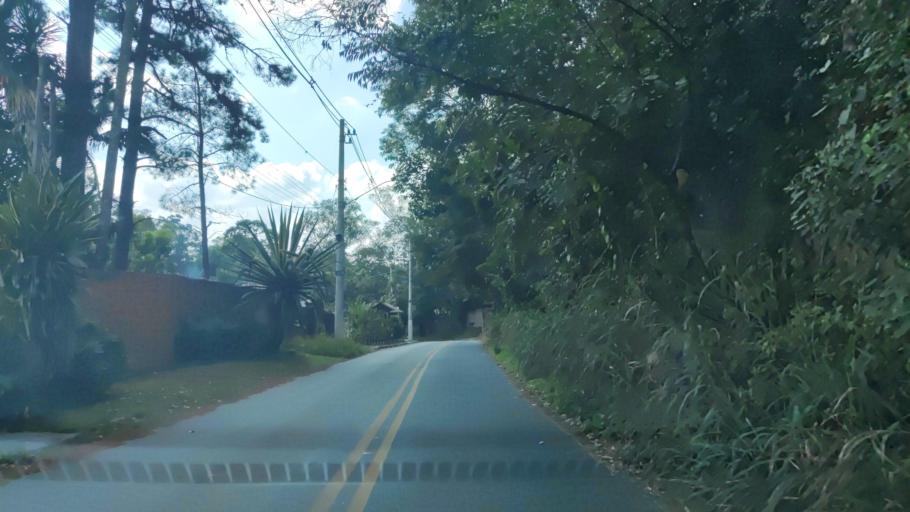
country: BR
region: Sao Paulo
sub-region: Itapecerica Da Serra
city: Itapecerica da Serra
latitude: -23.6987
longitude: -46.8434
